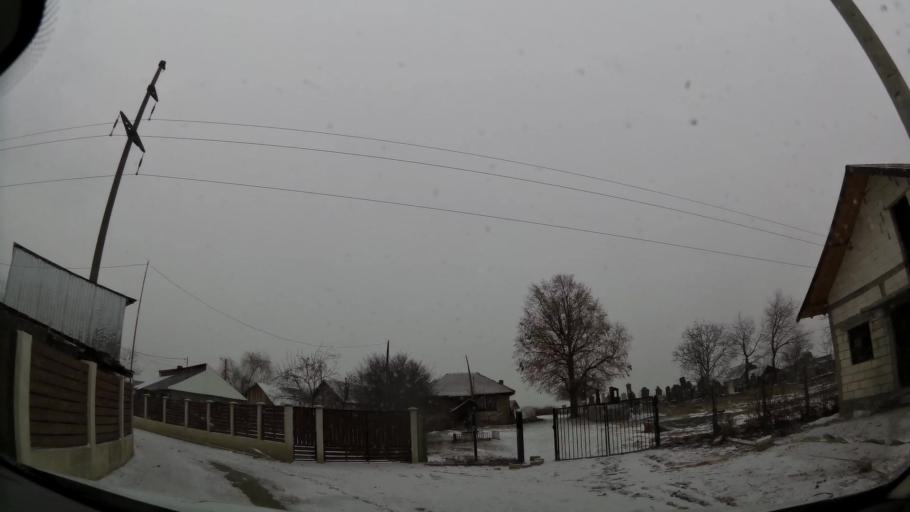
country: RO
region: Dambovita
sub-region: Municipiul Targoviste
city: Targoviste
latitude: 44.9309
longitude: 25.4302
